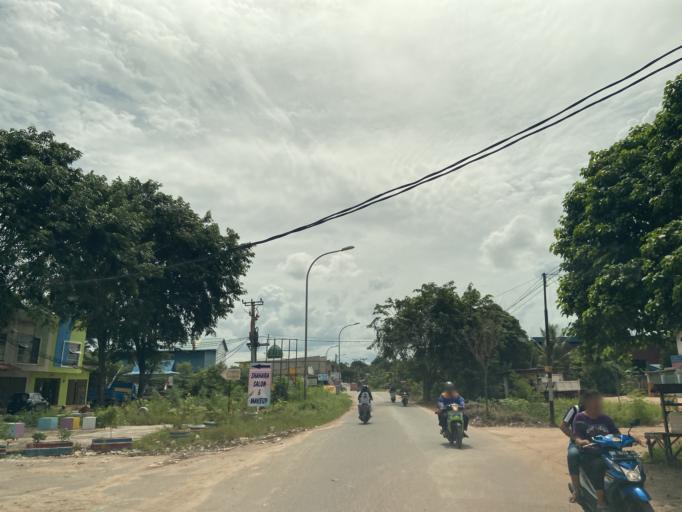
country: SG
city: Singapore
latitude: 1.0368
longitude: 103.9744
